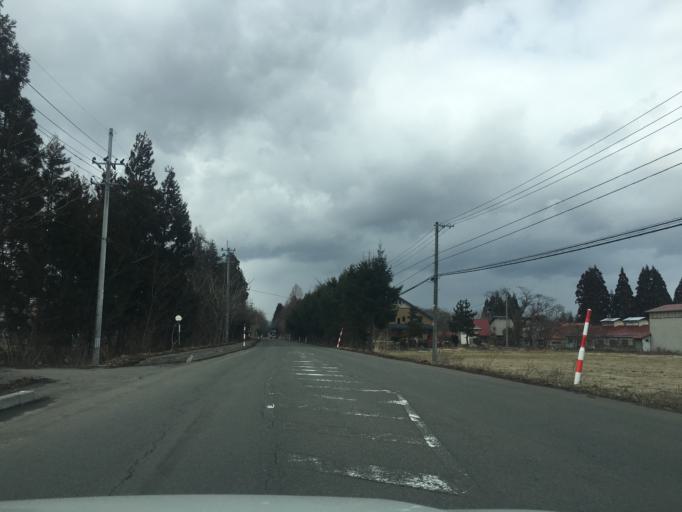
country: JP
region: Akita
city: Takanosu
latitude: 40.1781
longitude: 140.3471
